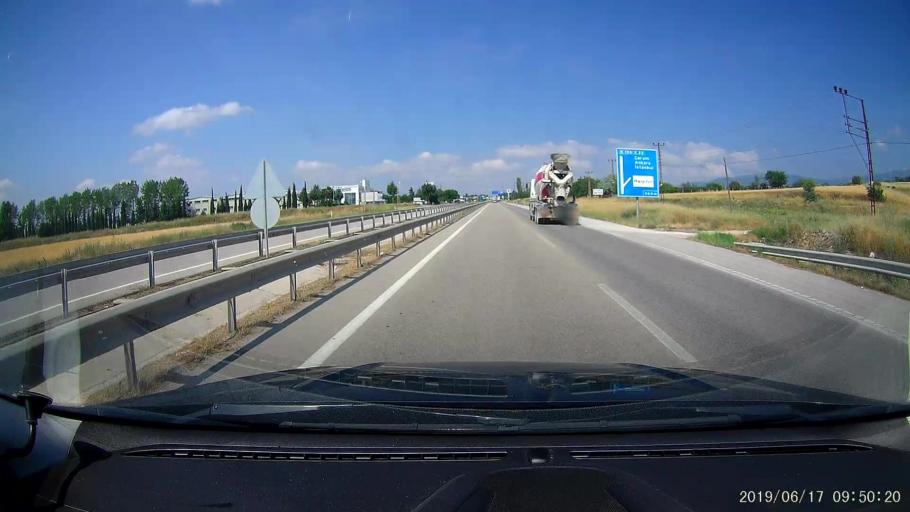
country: TR
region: Amasya
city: Merzifon
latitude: 40.8712
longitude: 35.5097
